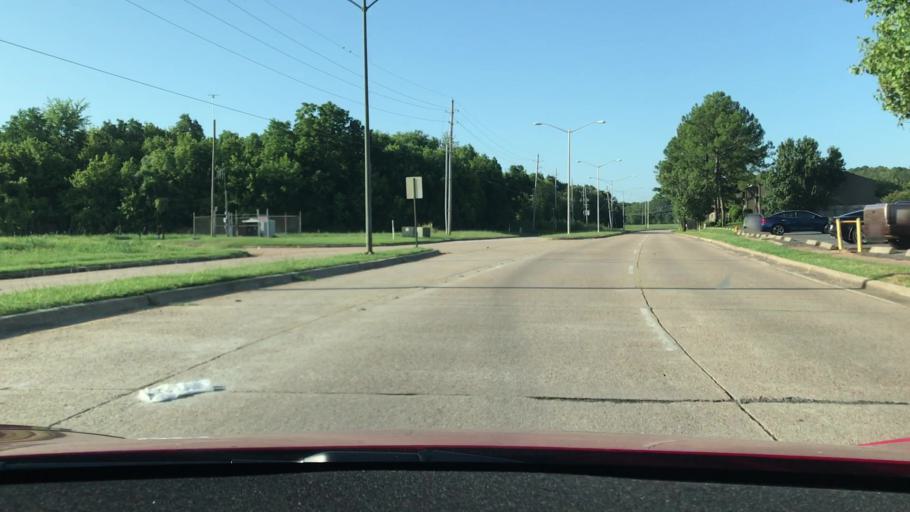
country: US
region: Louisiana
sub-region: Bossier Parish
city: Bossier City
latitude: 32.4405
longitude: -93.7280
